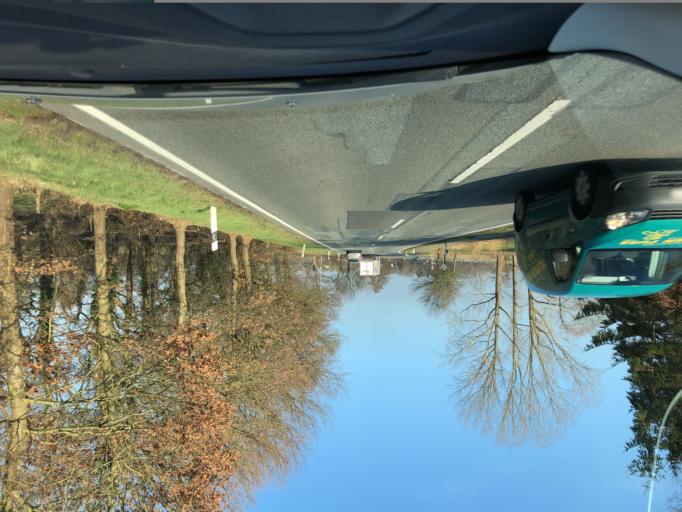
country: DE
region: Lower Saxony
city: Apen
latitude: 53.2997
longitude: 7.8025
